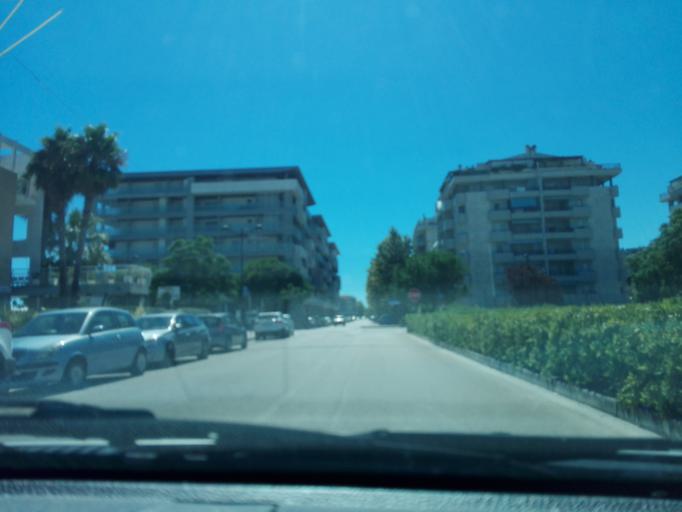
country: IT
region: Abruzzo
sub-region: Provincia di Pescara
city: Montesilvano Marina
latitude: 42.5223
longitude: 14.1532
